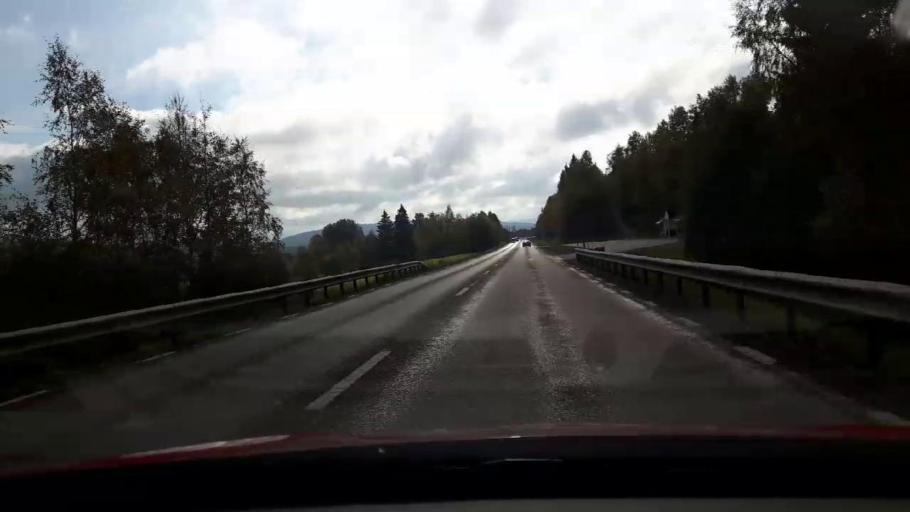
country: SE
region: Gaevleborg
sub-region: Ljusdals Kommun
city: Jaervsoe
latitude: 61.7346
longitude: 16.1627
